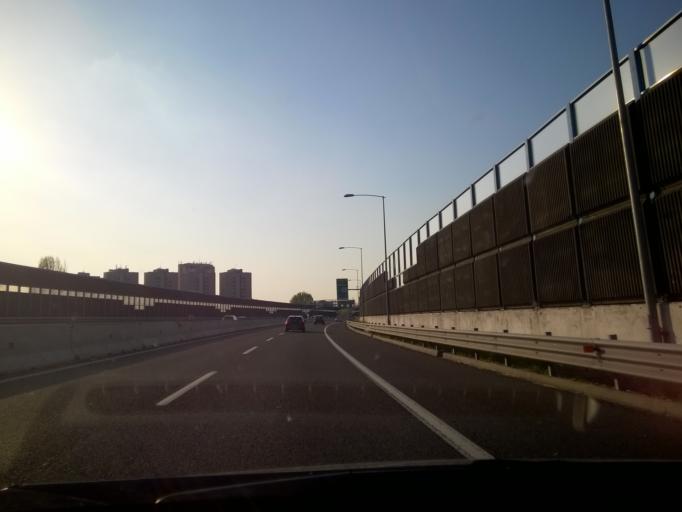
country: IT
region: Emilia-Romagna
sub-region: Provincia di Bologna
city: San Lazzaro
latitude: 44.4904
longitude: 11.3948
